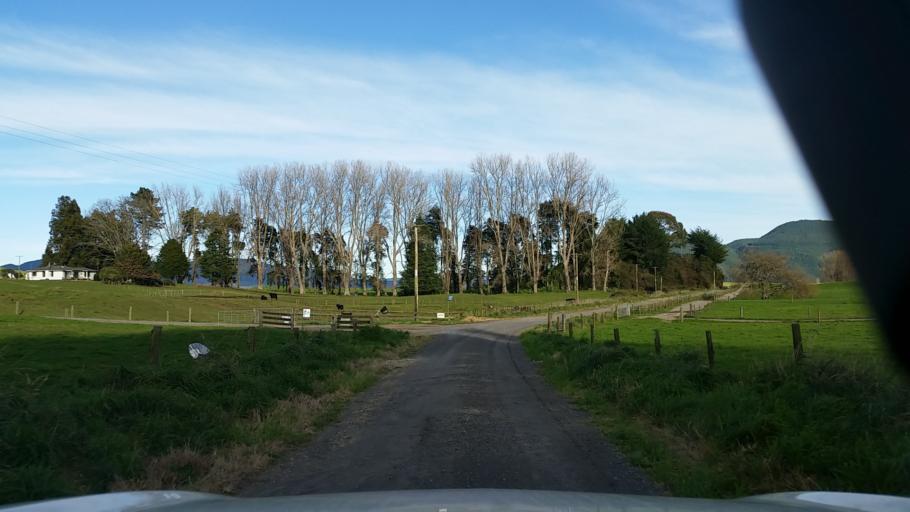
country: NZ
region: Waikato
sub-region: South Waikato District
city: Tokoroa
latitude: -38.3629
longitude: 176.0666
